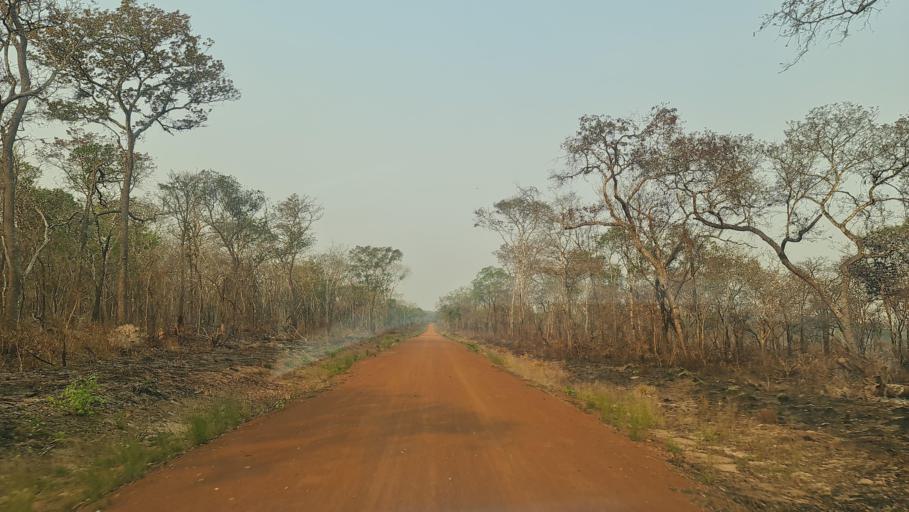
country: MZ
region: Zambezia
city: Quelimane
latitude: -17.1133
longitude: 37.1683
